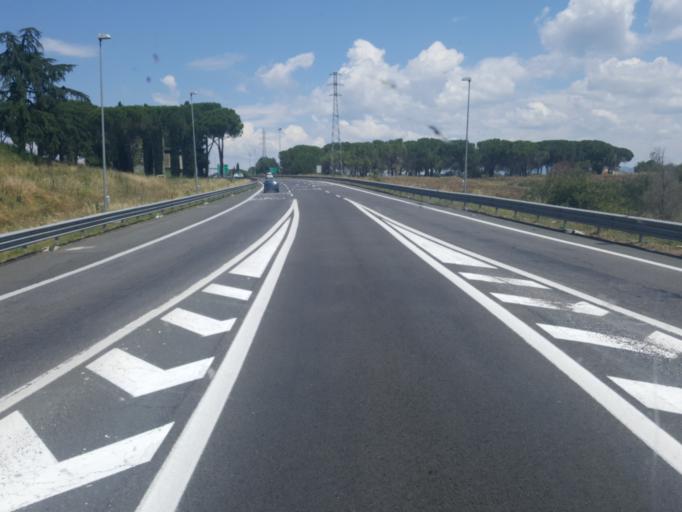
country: IT
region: Latium
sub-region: Citta metropolitana di Roma Capitale
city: Bivio di Capanelle
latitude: 42.1347
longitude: 12.6046
